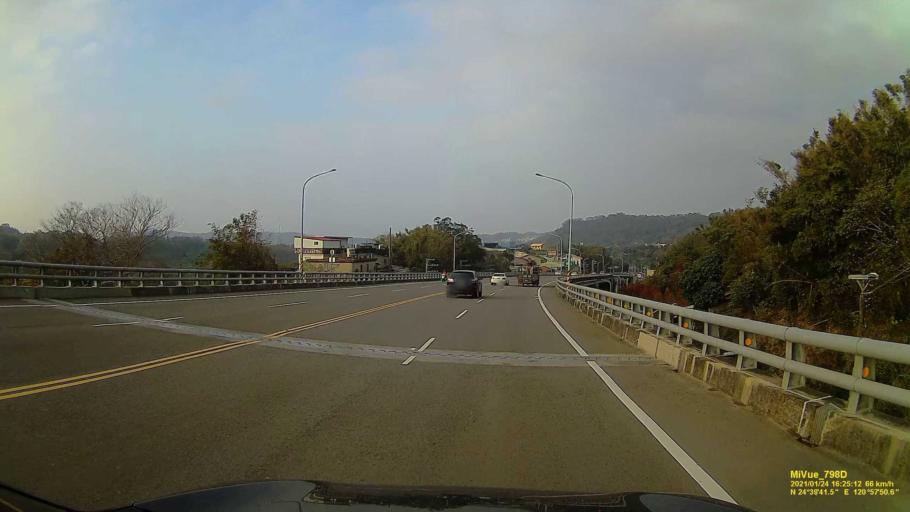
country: TW
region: Taiwan
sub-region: Hsinchu
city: Hsinchu
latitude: 24.6618
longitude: 120.9640
